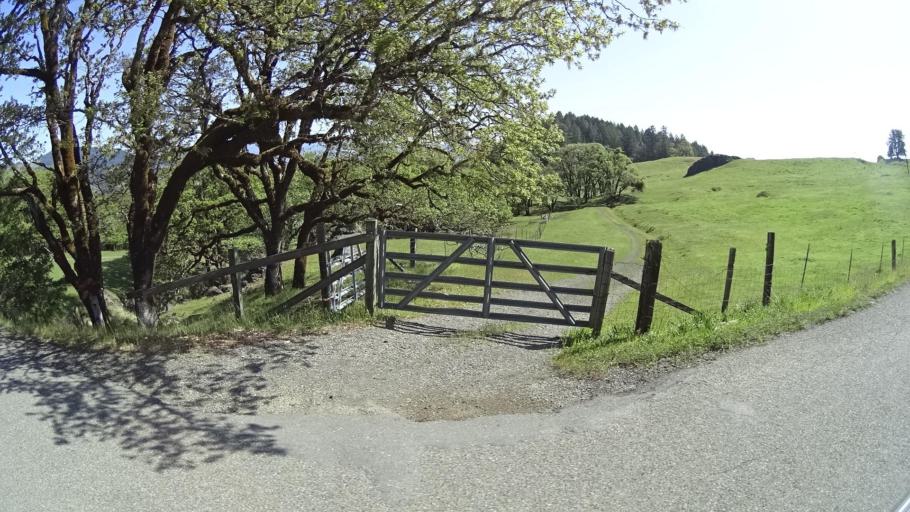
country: US
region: California
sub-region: Humboldt County
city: Redway
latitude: 40.0822
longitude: -123.6590
